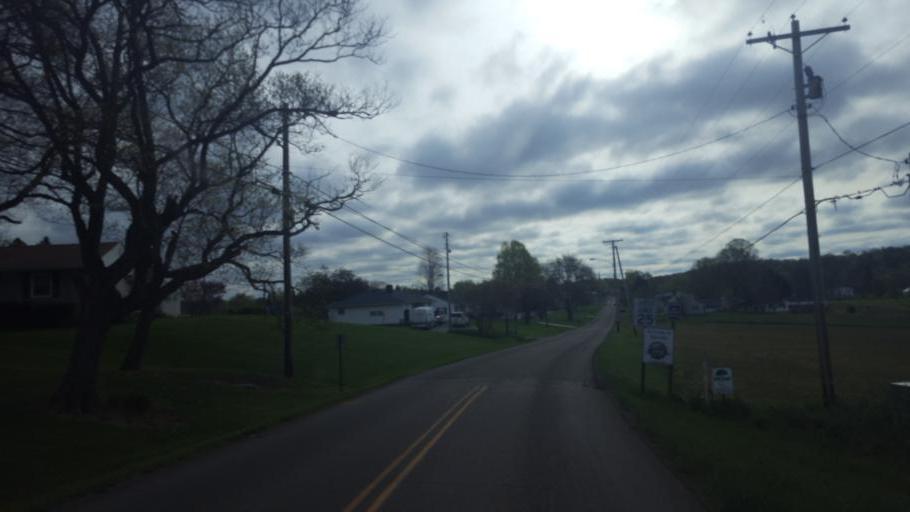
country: US
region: Ohio
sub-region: Knox County
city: Danville
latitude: 40.4481
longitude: -82.2705
